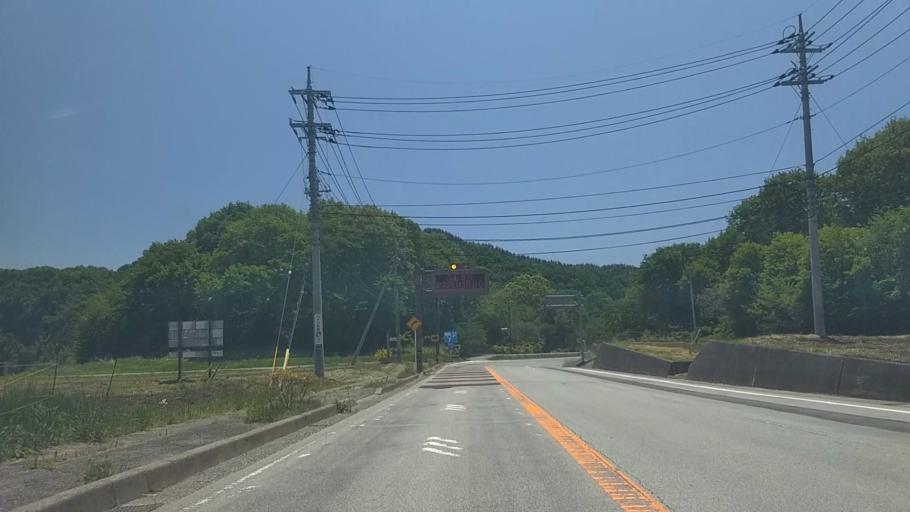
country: JP
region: Yamanashi
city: Nirasaki
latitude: 35.8793
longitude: 138.4398
